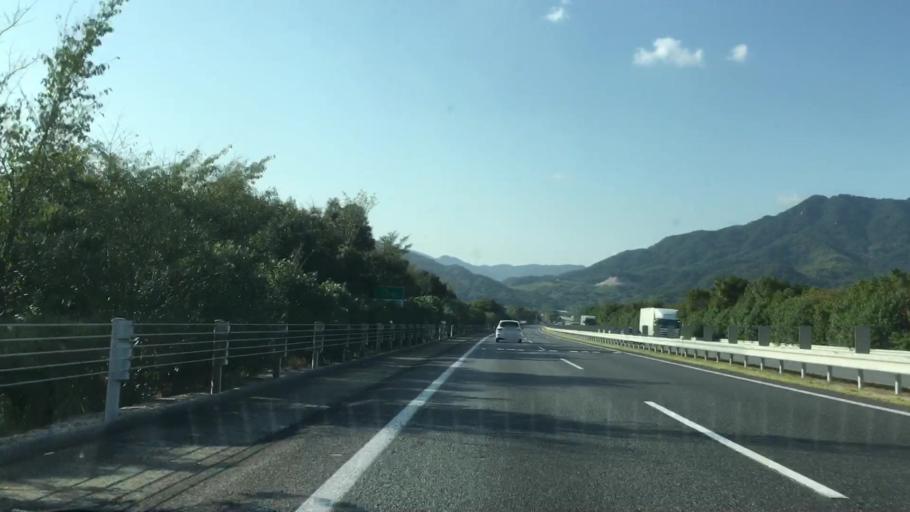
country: JP
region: Yamaguchi
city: Hofu
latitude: 34.0611
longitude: 131.6101
